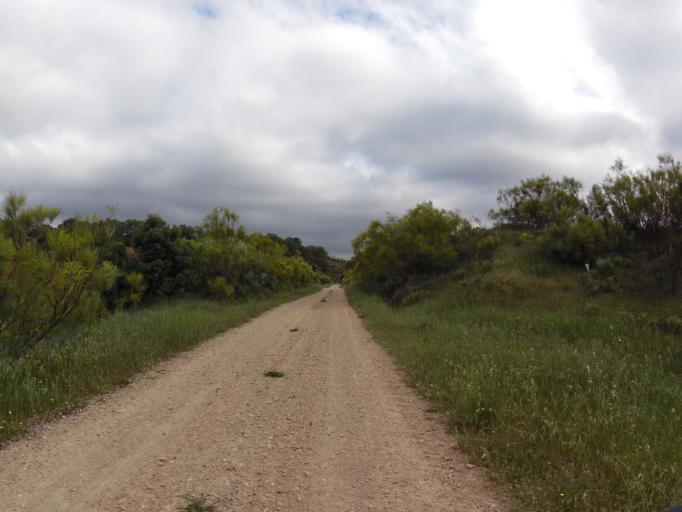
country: ES
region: Castille-La Mancha
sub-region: Provincia de Albacete
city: Robledo
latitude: 38.7245
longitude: -2.4785
